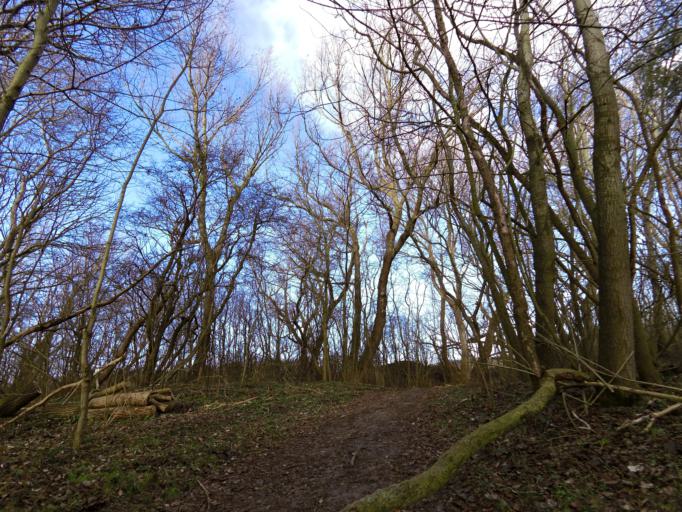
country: NL
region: South Holland
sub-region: Gemeente Hellevoetsluis
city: Nieuw-Helvoet
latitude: 51.8805
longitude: 4.0484
